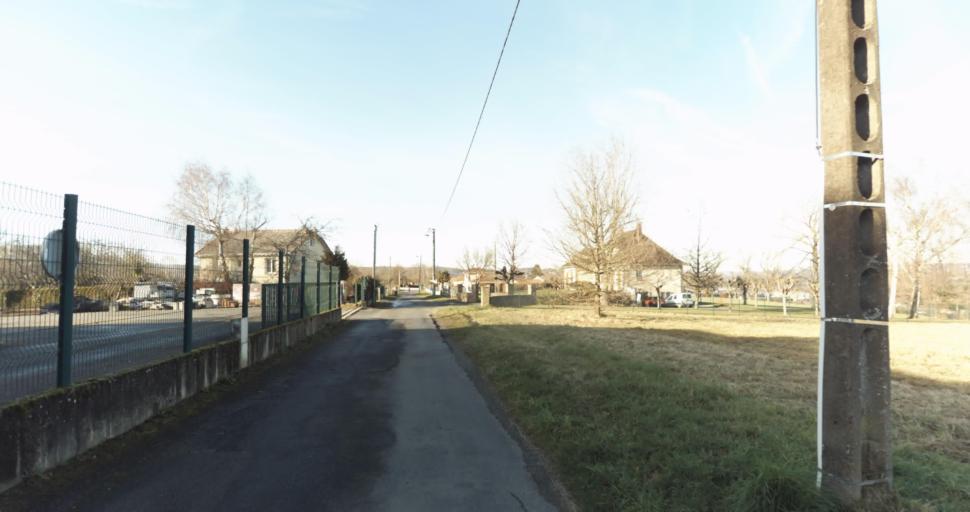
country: FR
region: Limousin
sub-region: Departement de la Haute-Vienne
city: Aixe-sur-Vienne
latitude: 45.7971
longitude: 1.1169
